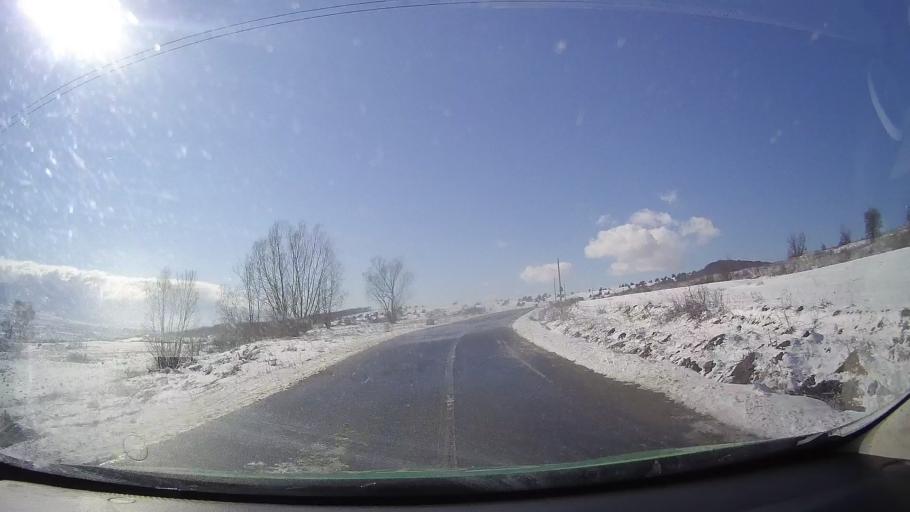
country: RO
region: Sibiu
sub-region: Comuna Avrig
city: Avrig
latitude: 45.7728
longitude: 24.3756
